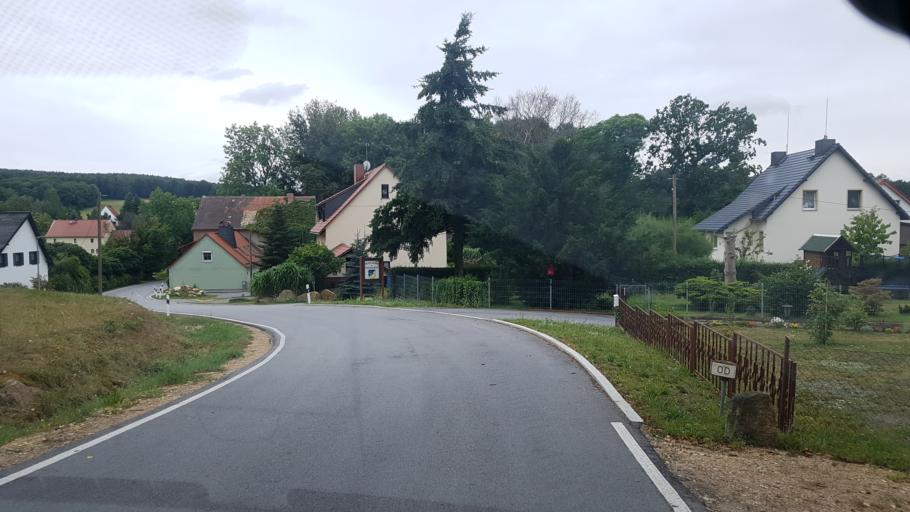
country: DE
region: Saxony
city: Konigshain
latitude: 51.2125
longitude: 14.8161
